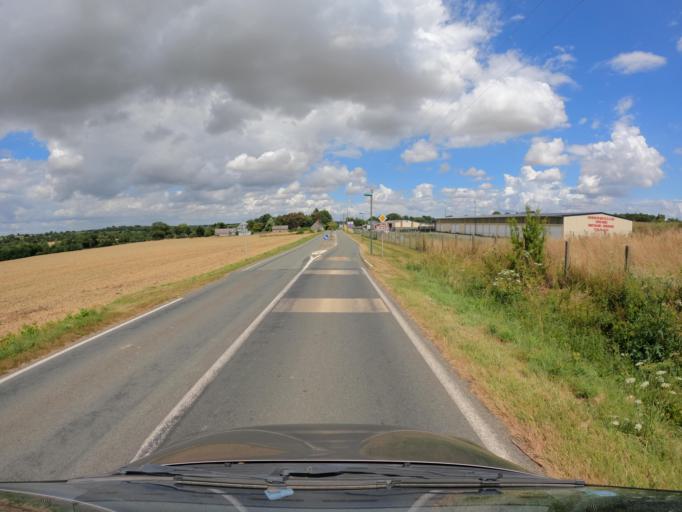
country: FR
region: Pays de la Loire
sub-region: Departement de Maine-et-Loire
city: Mire
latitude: 47.7510
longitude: -0.4992
